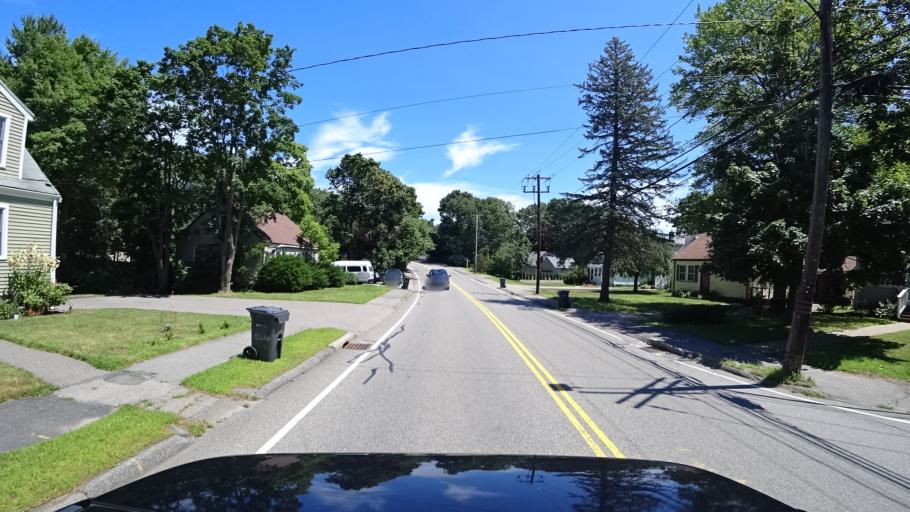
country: US
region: Massachusetts
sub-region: Norfolk County
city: Dedham
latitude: 42.2344
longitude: -71.1529
